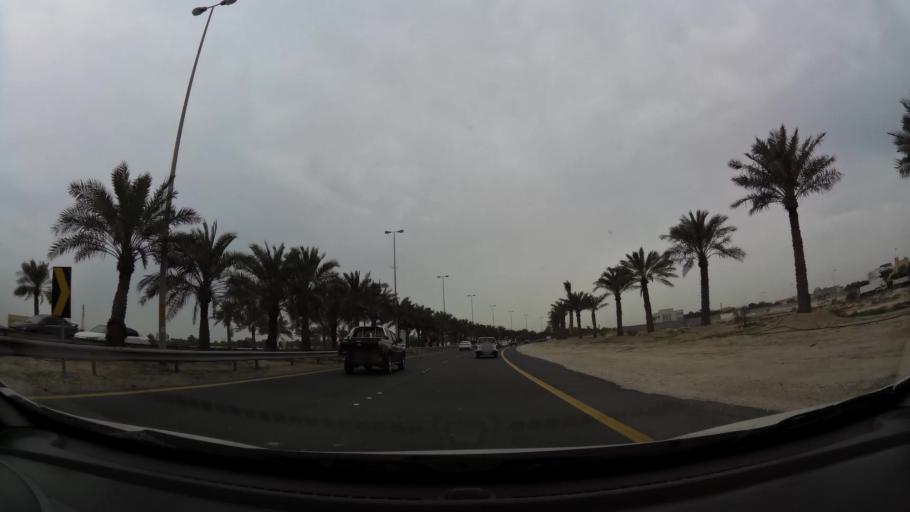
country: BH
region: Northern
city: Ar Rifa'
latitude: 26.1461
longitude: 50.5396
